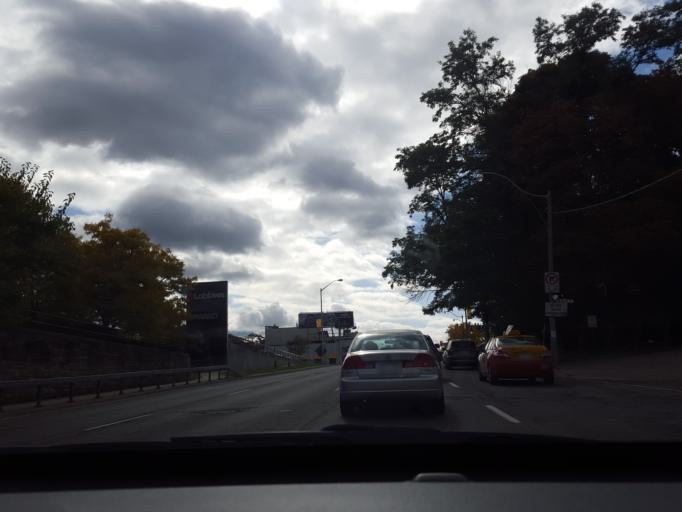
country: CA
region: Ontario
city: Willowdale
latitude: 43.7356
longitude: -79.4050
